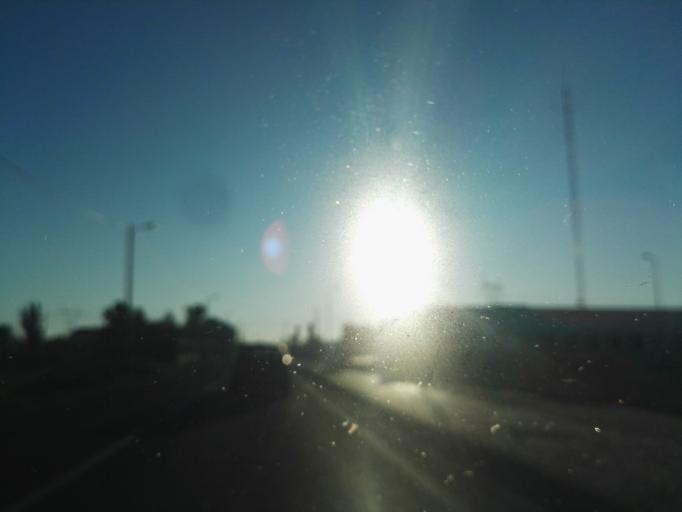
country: PT
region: Santarem
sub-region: Benavente
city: Samora Correia
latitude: 38.9292
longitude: -8.8783
